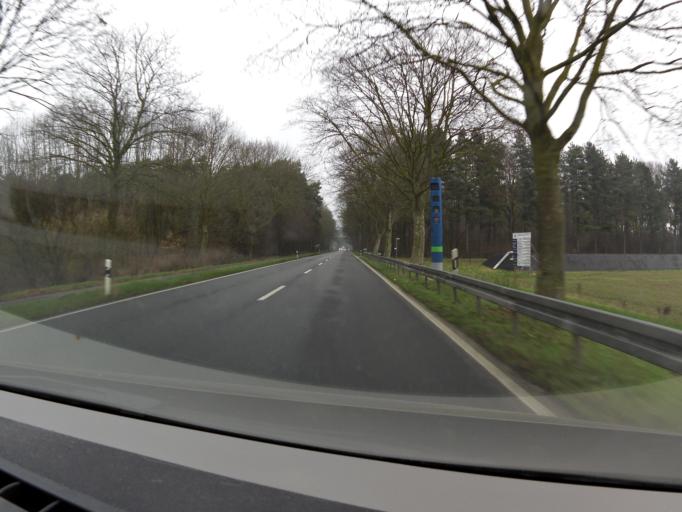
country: DE
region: North Rhine-Westphalia
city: Straelen
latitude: 51.4152
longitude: 6.2635
